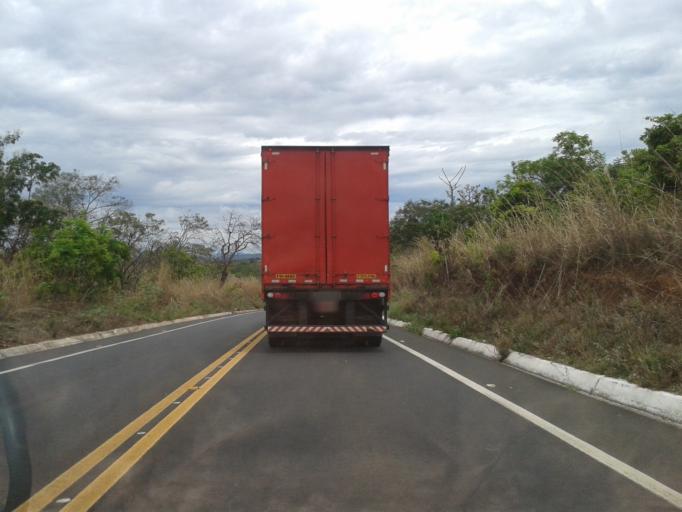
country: BR
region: Goias
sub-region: Caldas Novas
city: Caldas Novas
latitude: -17.8489
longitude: -48.6369
